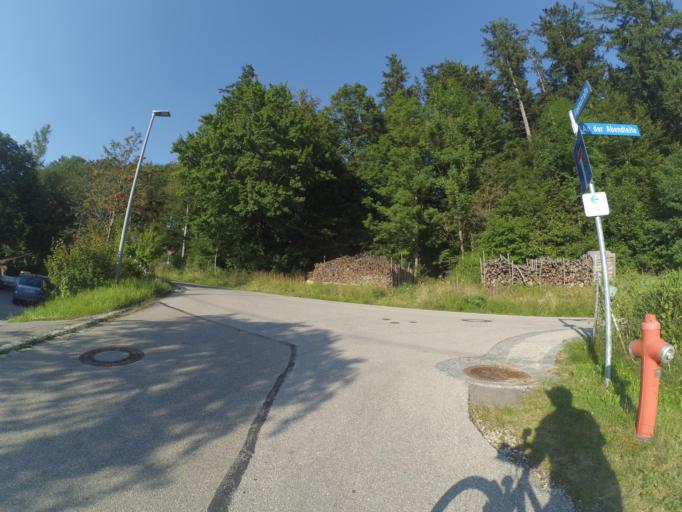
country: DE
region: Bavaria
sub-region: Swabia
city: Dirlewang
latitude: 48.0069
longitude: 10.5405
